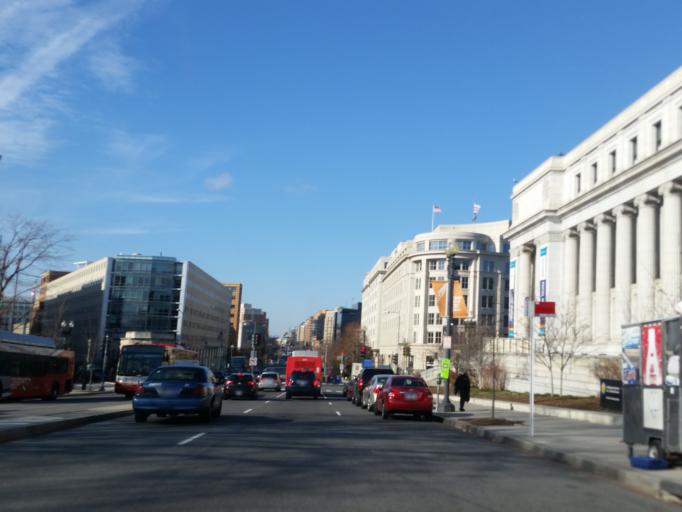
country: US
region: Washington, D.C.
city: Washington, D.C.
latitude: 38.8971
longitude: -77.0081
